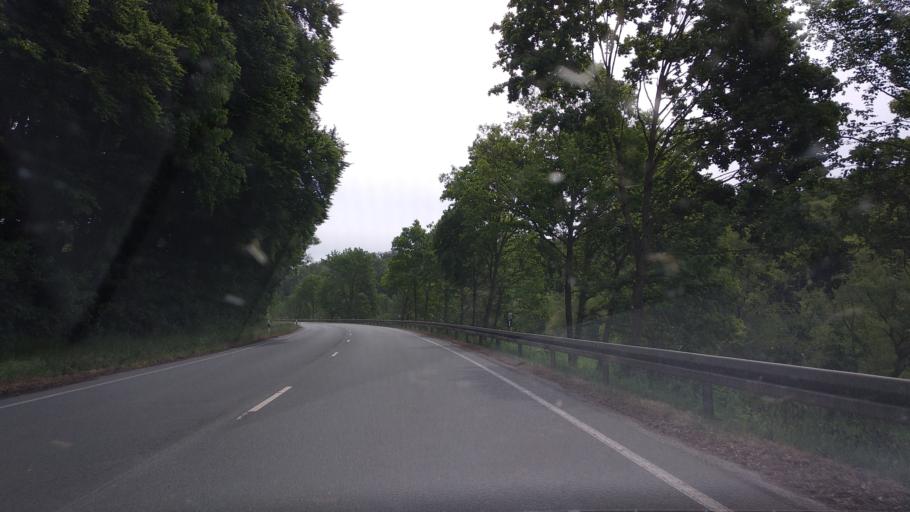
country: DE
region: North Rhine-Westphalia
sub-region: Regierungsbezirk Detmold
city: Willebadessen
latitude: 51.6244
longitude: 9.0894
